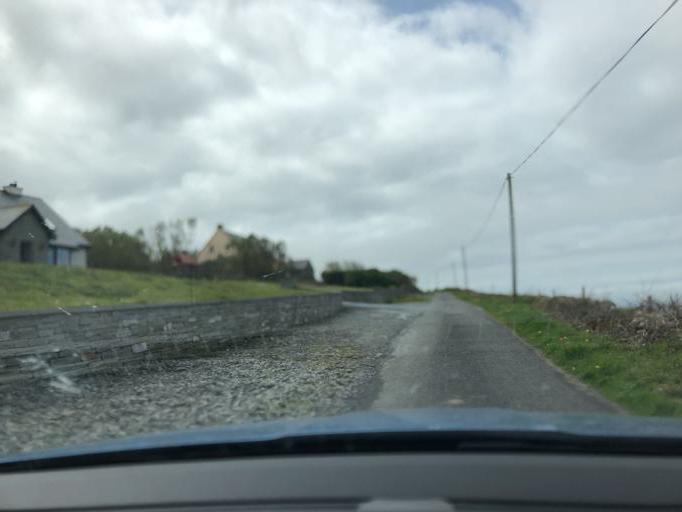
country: IE
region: Connaught
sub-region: County Galway
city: Bearna
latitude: 53.0000
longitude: -9.3959
